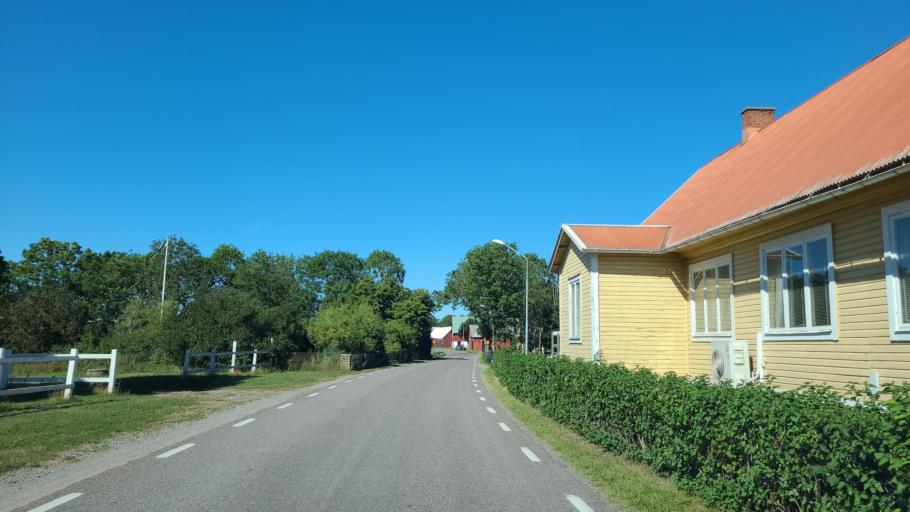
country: SE
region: Kalmar
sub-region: Borgholms Kommun
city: Borgholm
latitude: 56.8741
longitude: 16.8222
